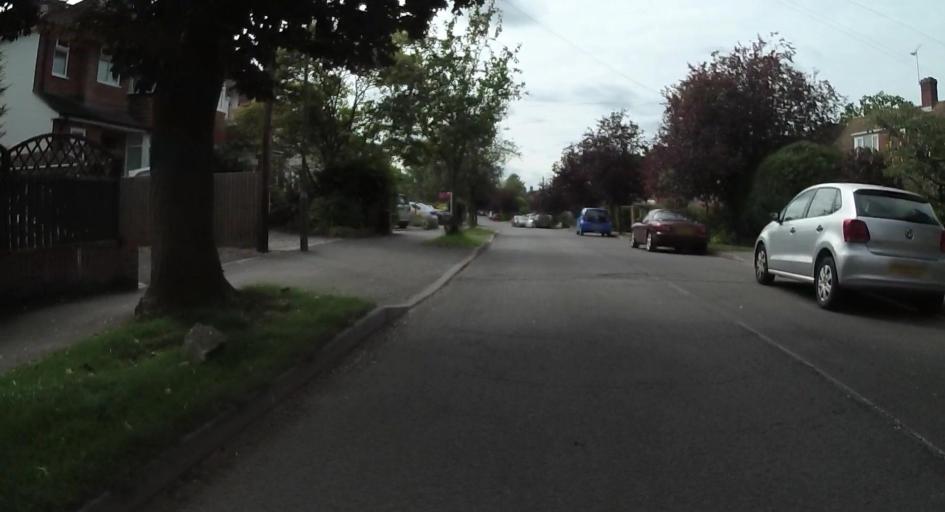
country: GB
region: England
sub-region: Surrey
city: Woking
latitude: 51.3271
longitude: -0.5711
